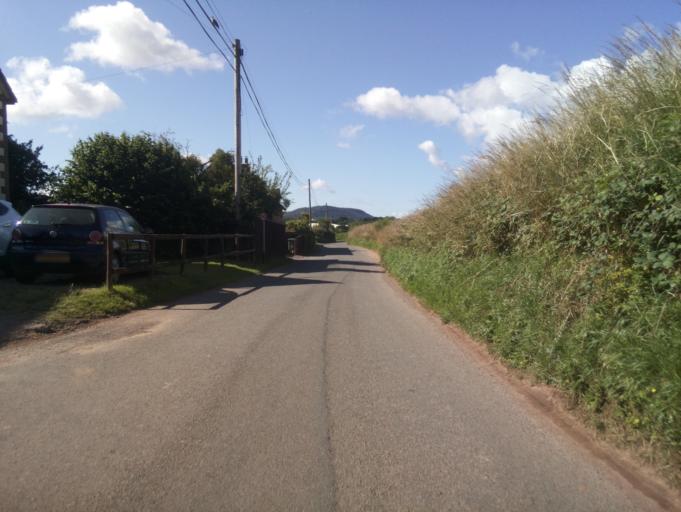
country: GB
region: England
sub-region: Herefordshire
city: Ross on Wye
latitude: 51.9328
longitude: -2.5778
